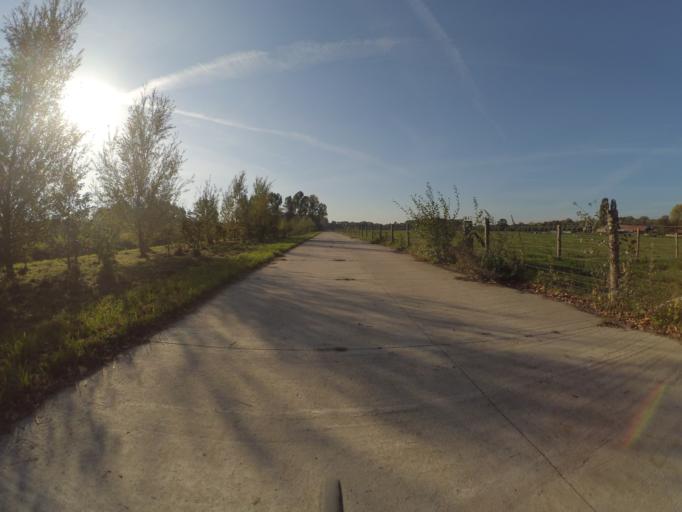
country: NL
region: Utrecht
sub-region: Gemeente Bunnik
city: Bunnik
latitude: 52.0825
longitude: 5.1900
